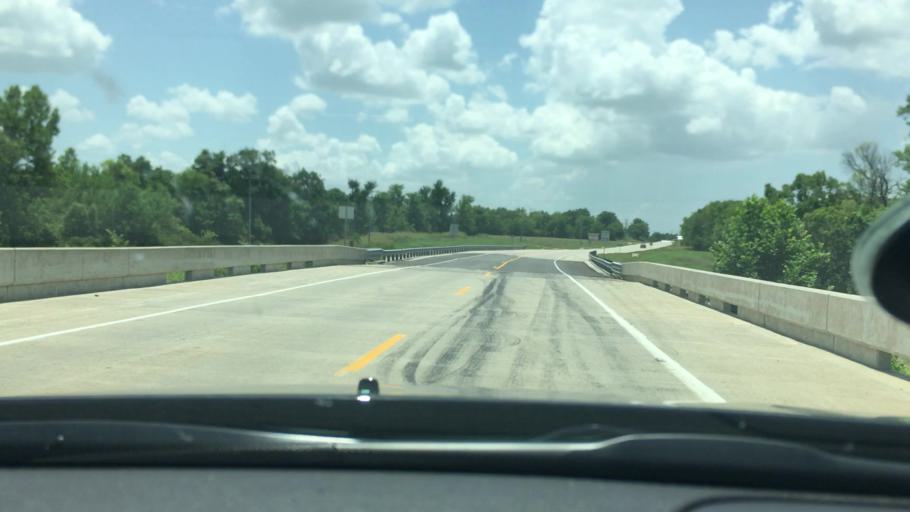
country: US
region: Oklahoma
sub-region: Johnston County
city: Tishomingo
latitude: 34.4544
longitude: -96.6358
